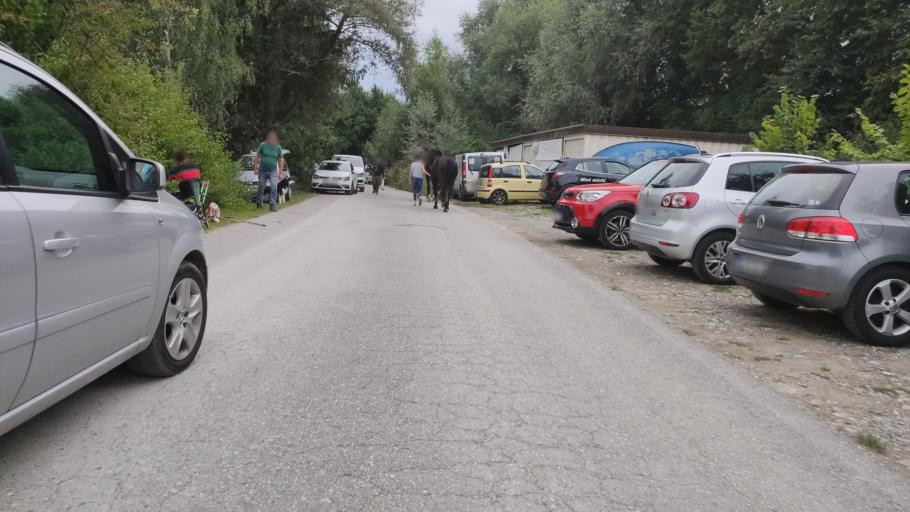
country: DE
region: Bavaria
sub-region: Swabia
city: Konigsbrunn
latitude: 48.2462
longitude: 10.8821
